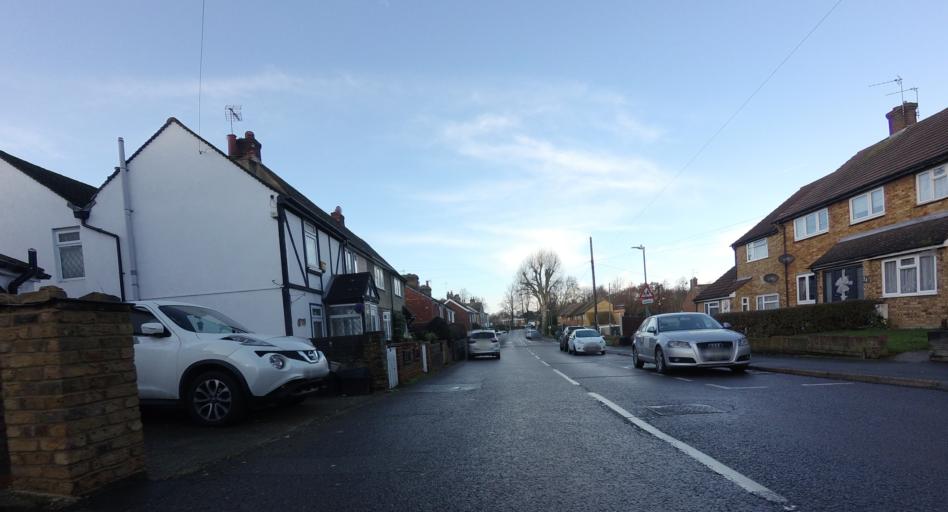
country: GB
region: England
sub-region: Kent
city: Dartford
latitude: 51.4270
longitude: 0.1982
